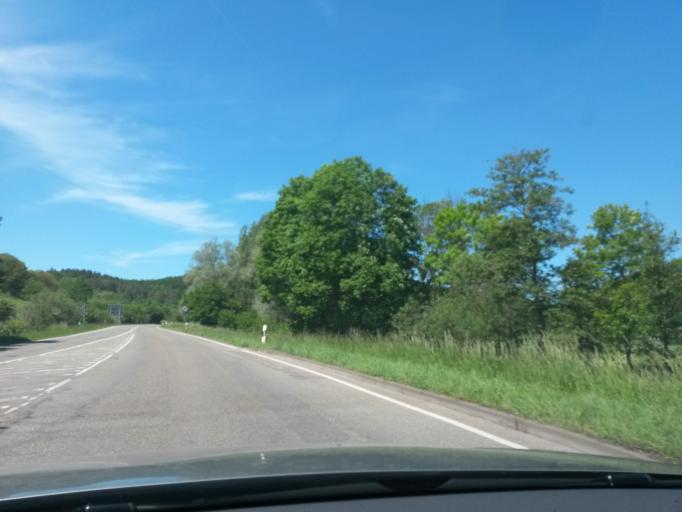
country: DE
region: Baden-Wuerttemberg
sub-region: Regierungsbezirk Stuttgart
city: Weil der Stadt
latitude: 48.7265
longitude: 8.8889
